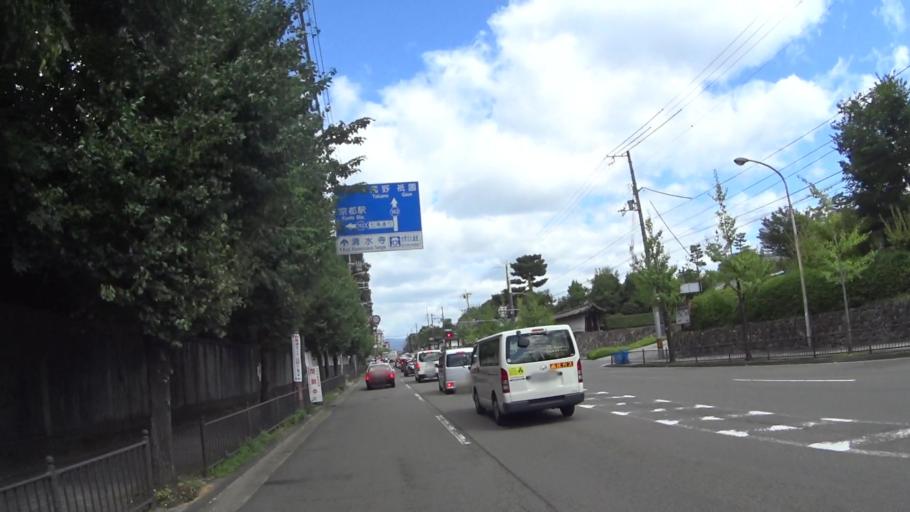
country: JP
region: Kyoto
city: Kyoto
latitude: 34.9877
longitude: 135.7743
